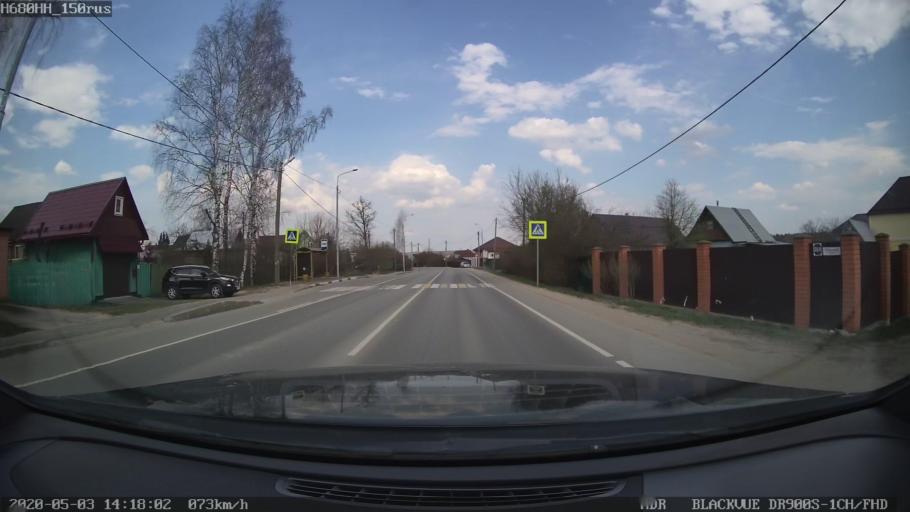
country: RU
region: Moskovskaya
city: Solnechnogorsk
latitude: 56.2142
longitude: 36.9718
